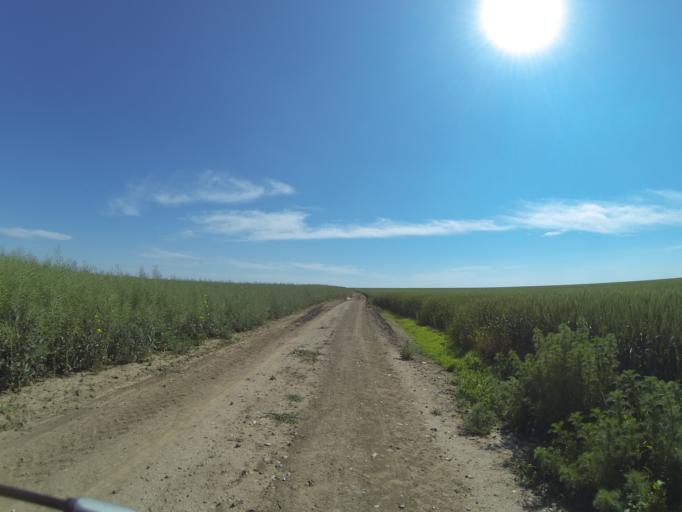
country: RO
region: Dolj
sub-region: Comuna Cosoveni
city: Cosoveni
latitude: 44.2569
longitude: 23.9984
